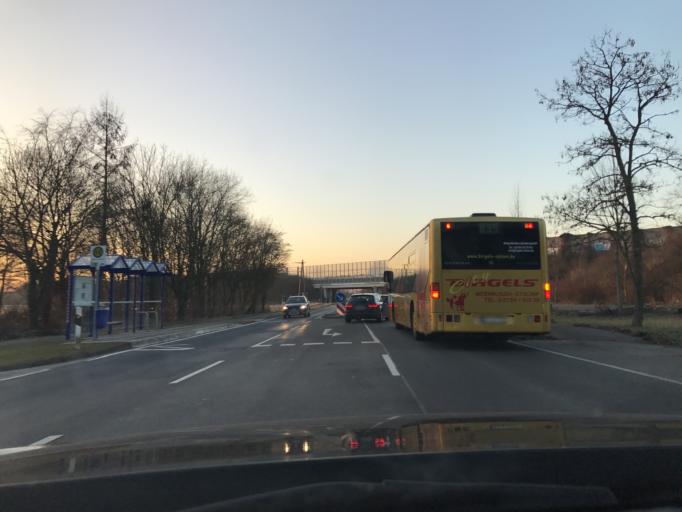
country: DE
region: North Rhine-Westphalia
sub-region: Regierungsbezirk Dusseldorf
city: Meerbusch
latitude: 51.2918
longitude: 6.6475
